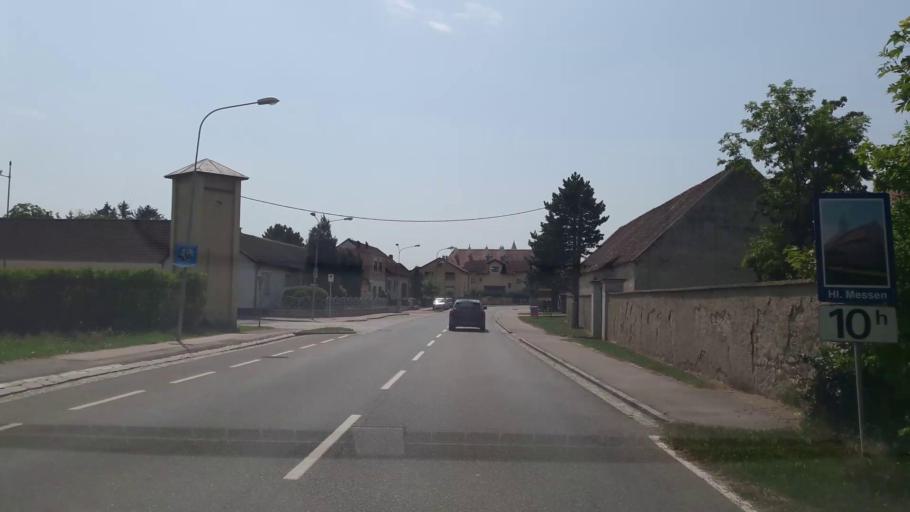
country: AT
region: Lower Austria
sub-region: Politischer Bezirk Wien-Umgebung
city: Schwadorf
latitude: 48.0520
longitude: 16.6073
